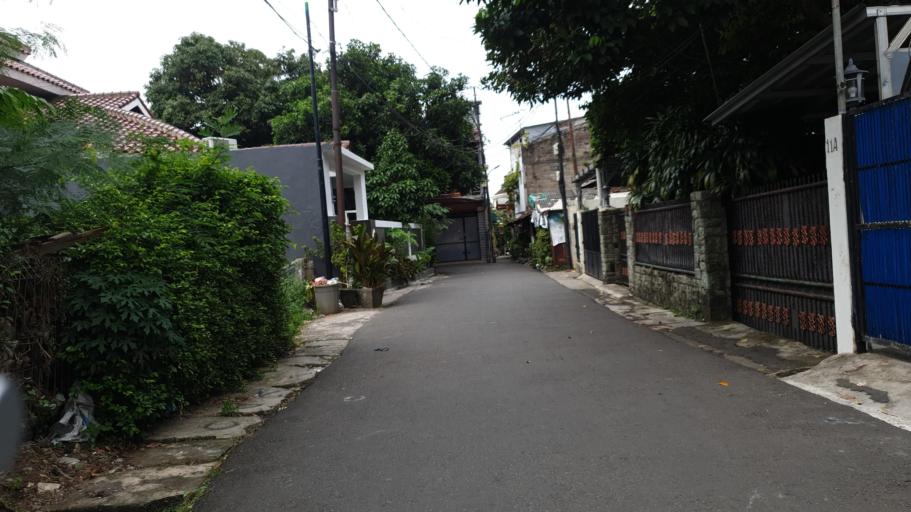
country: ID
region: Banten
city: South Tangerang
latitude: -6.2868
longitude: 106.7917
